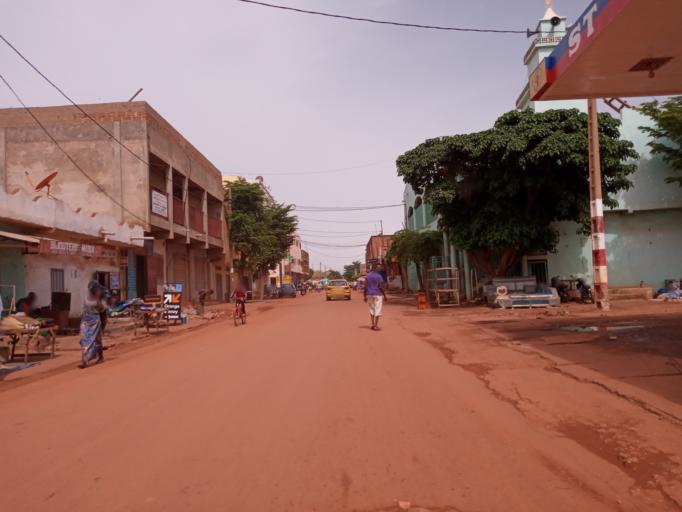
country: ML
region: Bamako
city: Bamako
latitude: 12.5537
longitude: -7.9937
